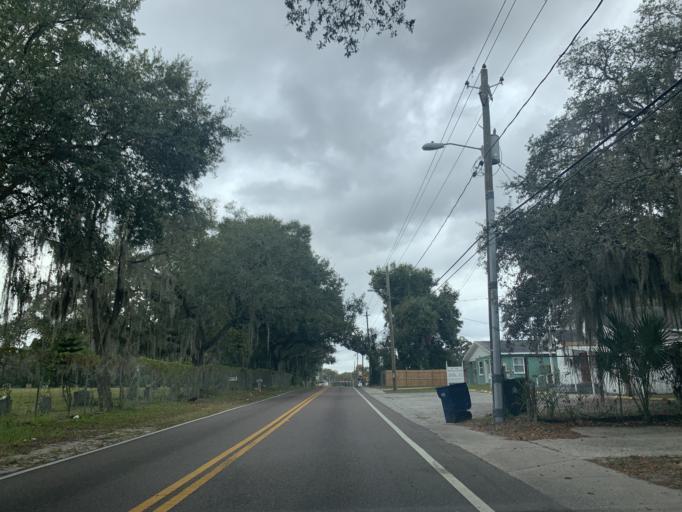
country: US
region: Florida
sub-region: Hillsborough County
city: East Lake-Orient Park
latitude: 27.9852
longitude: -82.4104
